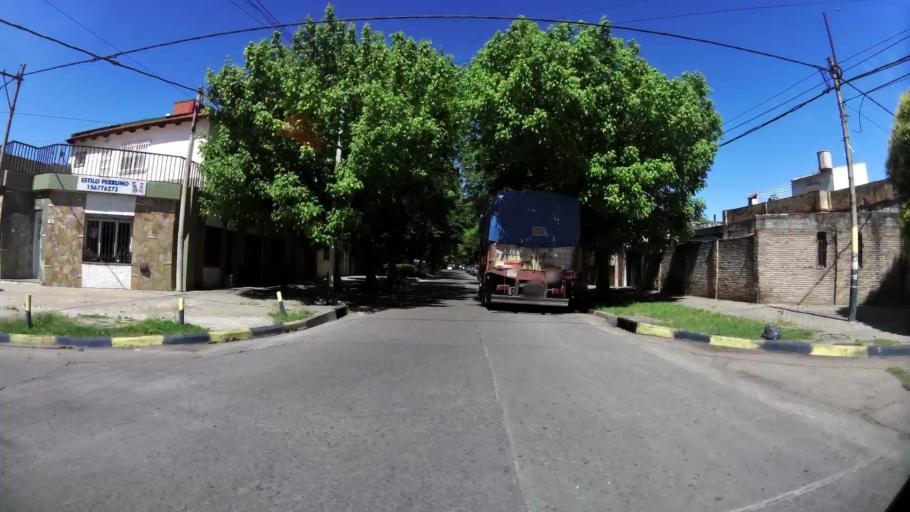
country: AR
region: Santa Fe
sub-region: Departamento de Rosario
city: Rosario
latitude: -32.9365
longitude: -60.6813
